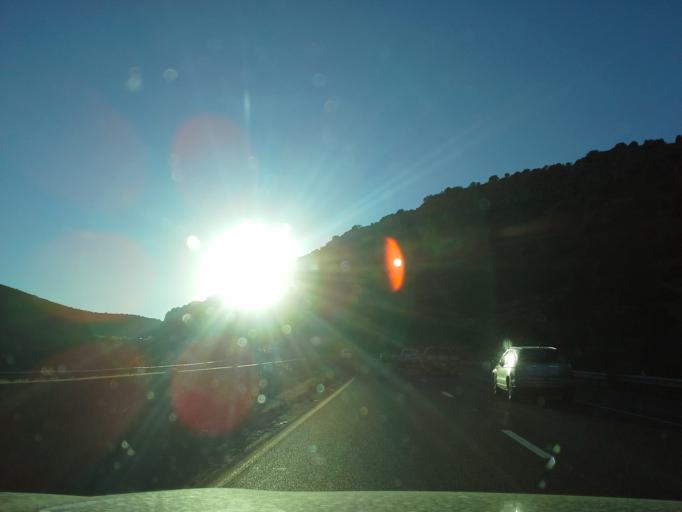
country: US
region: Arizona
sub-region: Yavapai County
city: Camp Verde
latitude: 34.5348
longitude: -111.9368
